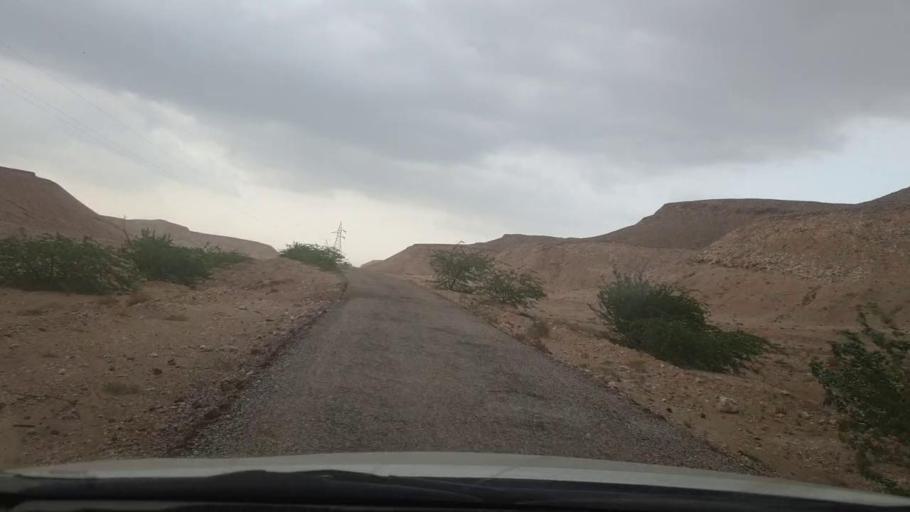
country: PK
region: Sindh
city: Khairpur
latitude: 27.4654
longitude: 68.9239
